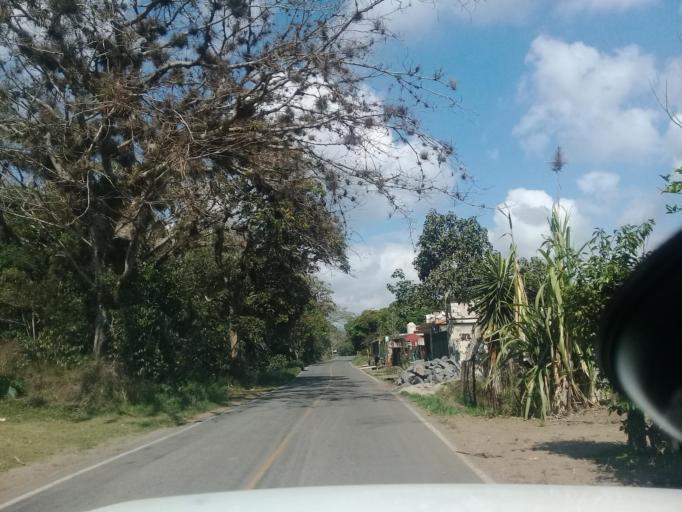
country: MX
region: Veracruz
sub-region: Coatepec
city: Bella Esperanza
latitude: 19.4372
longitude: -96.8684
